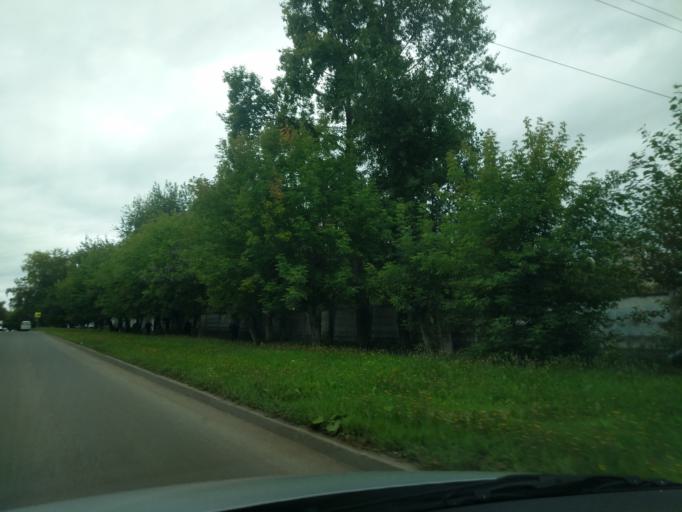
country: RU
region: Kirov
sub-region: Kirovo-Chepetskiy Rayon
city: Kirov
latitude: 58.6352
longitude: 49.6157
